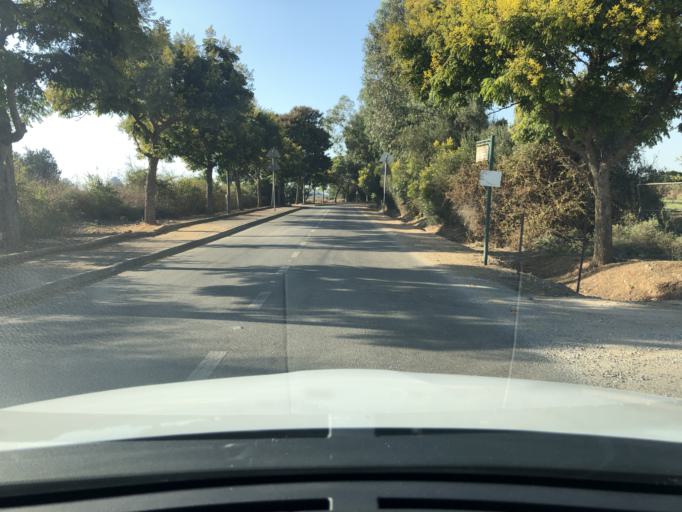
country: IL
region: Central District
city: Hod HaSharon
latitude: 32.1348
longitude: 34.9086
